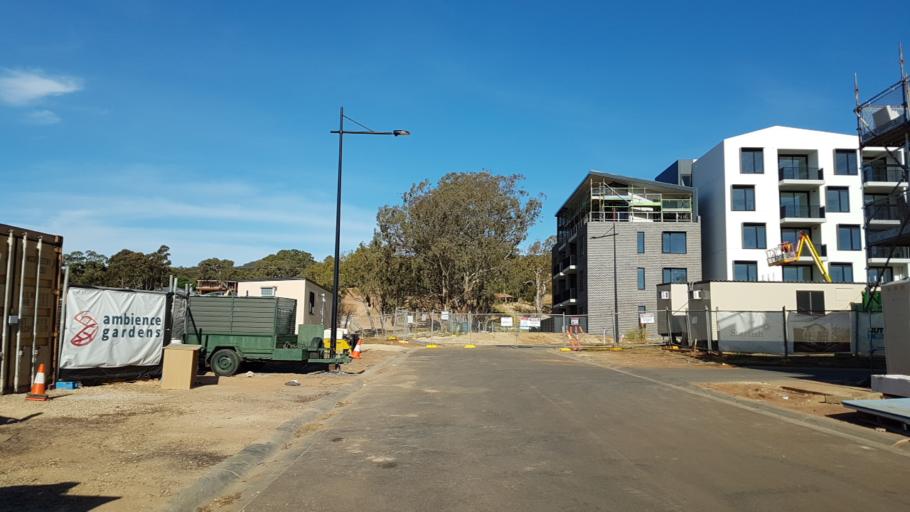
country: AU
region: South Australia
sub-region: Adelaide Hills
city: Adelaide Hills
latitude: -34.9054
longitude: 138.6866
